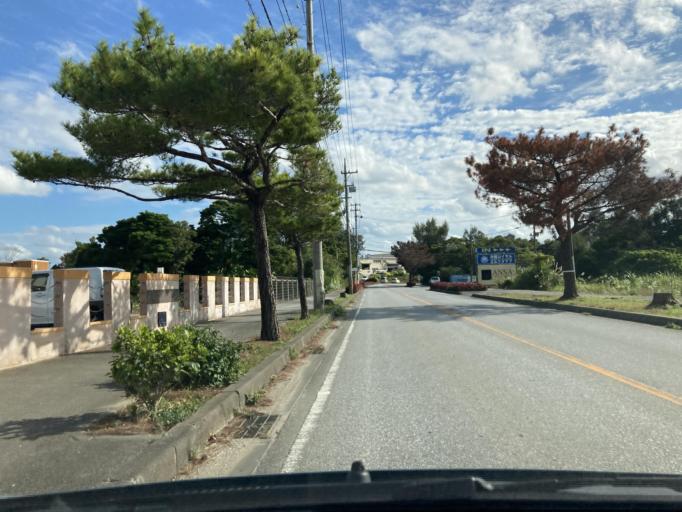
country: JP
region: Okinawa
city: Ishikawa
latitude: 26.4305
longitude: 127.8072
